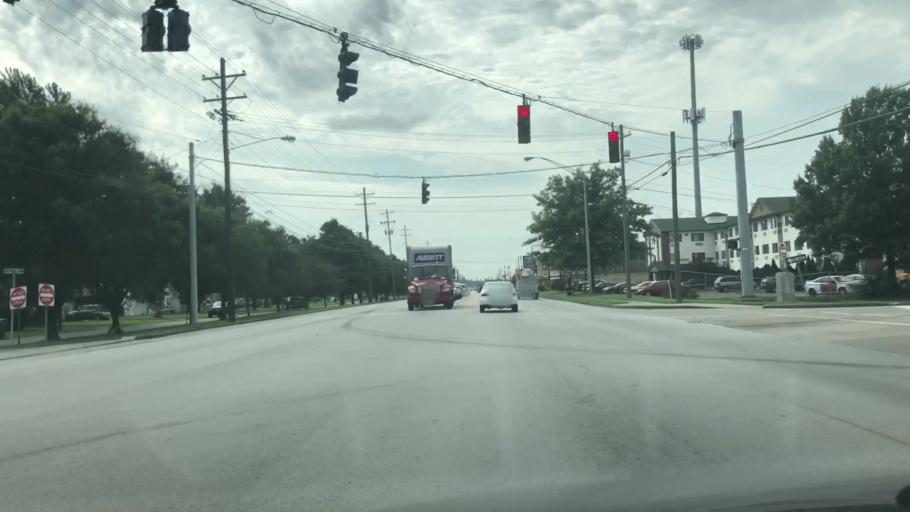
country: US
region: Kentucky
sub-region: Jefferson County
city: Audubon Park
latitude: 38.1789
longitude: -85.7173
